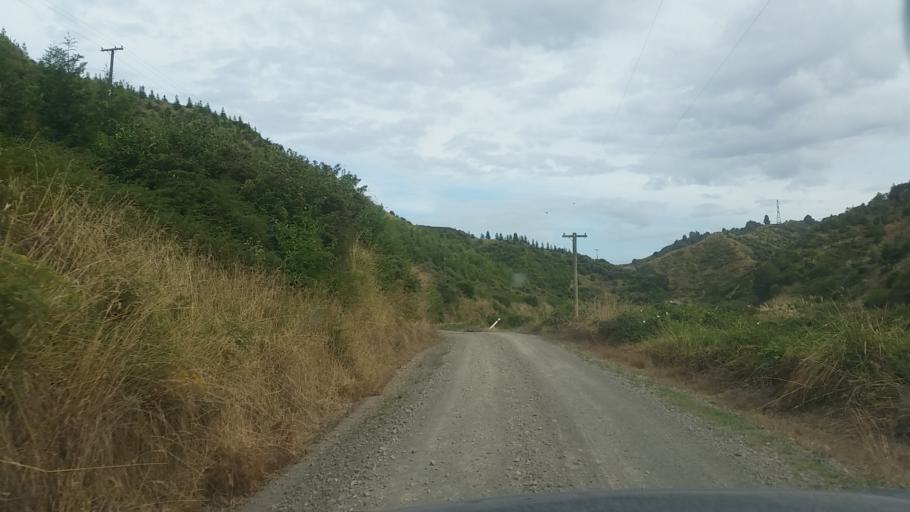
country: NZ
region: Taranaki
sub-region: New Plymouth District
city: Waitara
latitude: -39.1415
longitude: 174.7196
